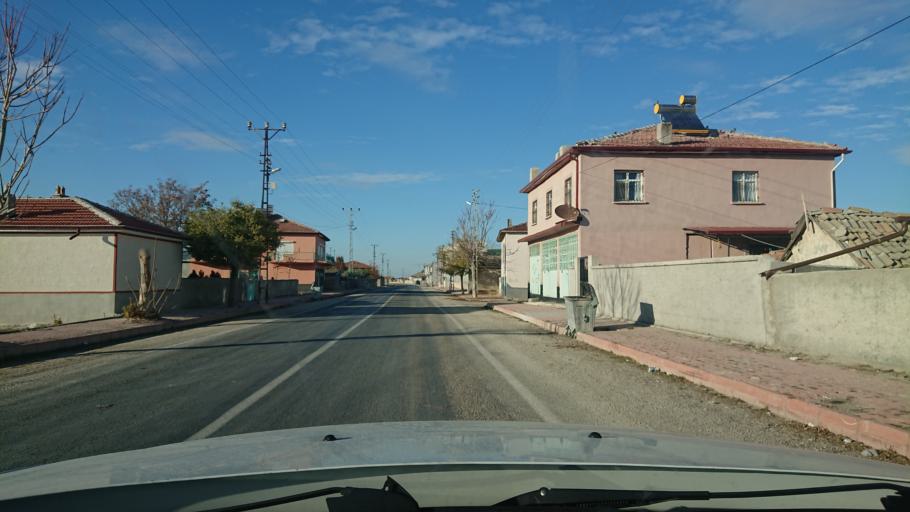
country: TR
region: Aksaray
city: Eskil
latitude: 38.5626
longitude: 33.1949
